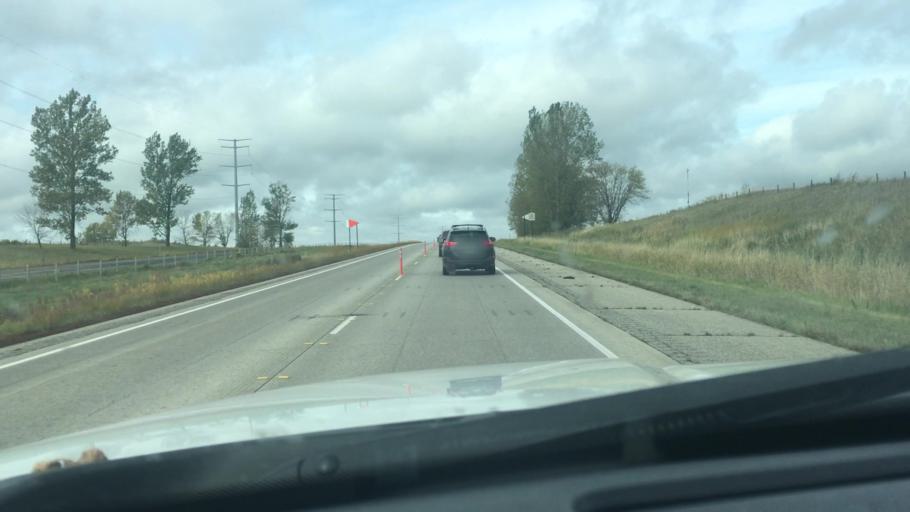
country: US
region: Minnesota
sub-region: Douglas County
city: Alexandria
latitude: 45.9118
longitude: -95.5421
